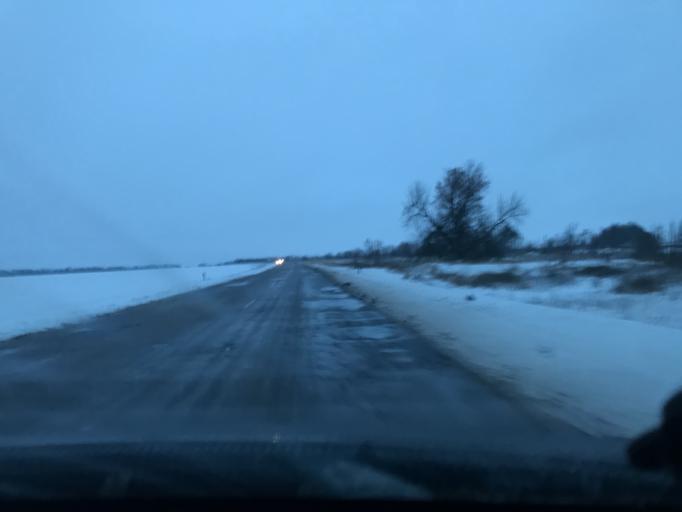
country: RU
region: Rostov
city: Letnik
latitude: 45.9923
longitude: 41.2244
